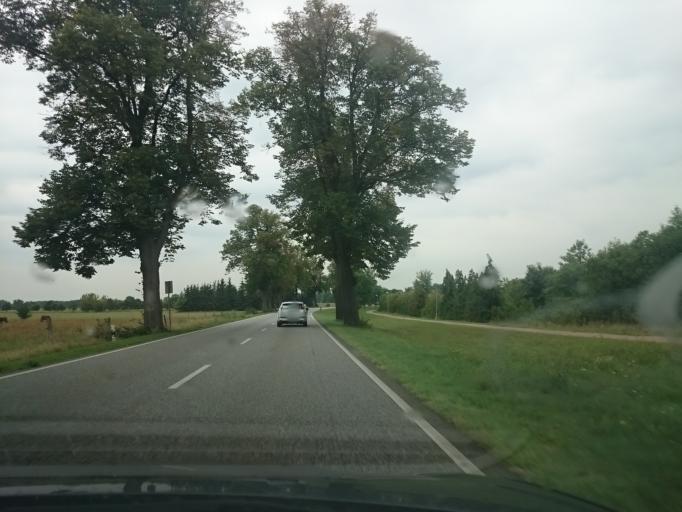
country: DE
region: Brandenburg
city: Gransee
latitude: 53.0357
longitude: 13.1925
